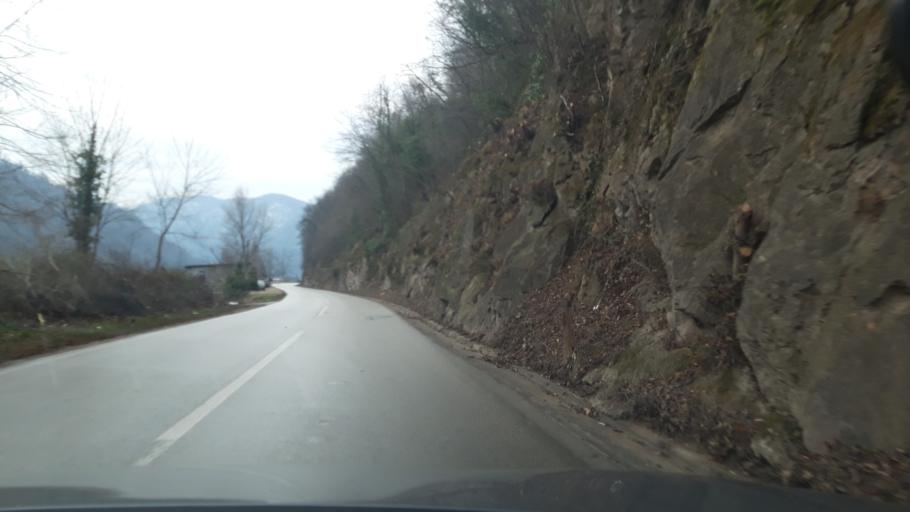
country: RS
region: Central Serbia
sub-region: Macvanski Okrug
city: Mali Zvornik
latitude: 44.3518
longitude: 19.1085
